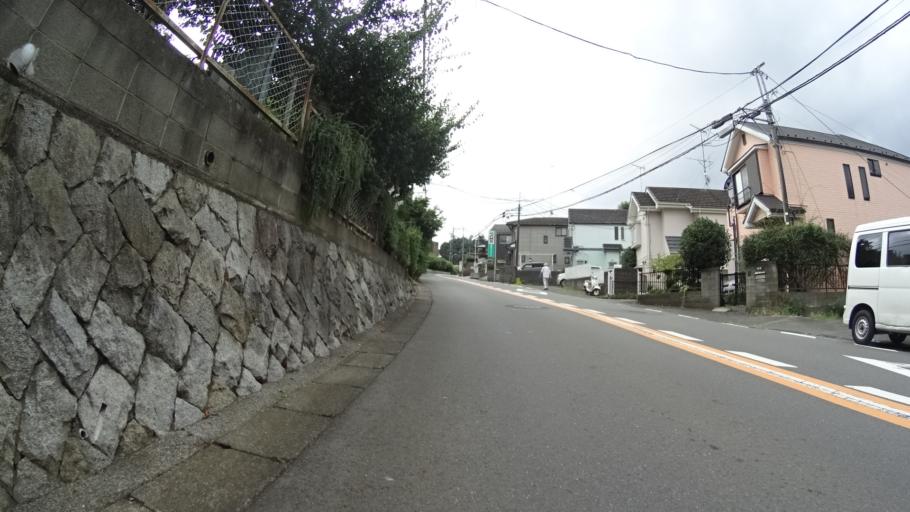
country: JP
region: Tokyo
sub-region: Machida-shi
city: Machida
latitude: 35.5933
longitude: 139.3971
